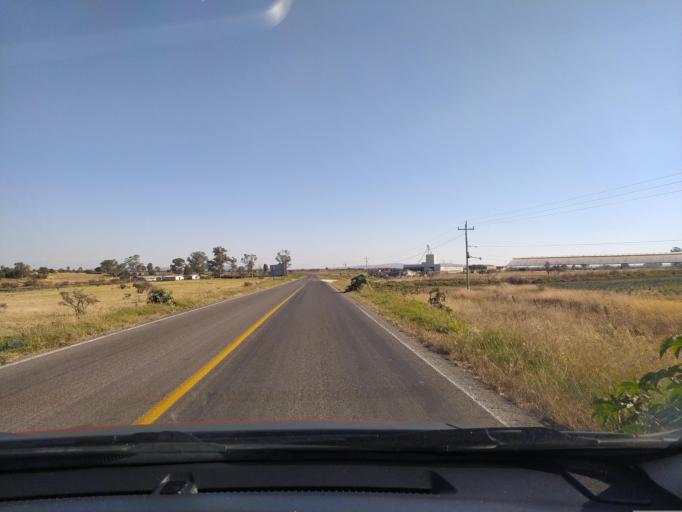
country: MX
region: Jalisco
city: Valle de Guadalupe
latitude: 21.0266
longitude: -102.5487
